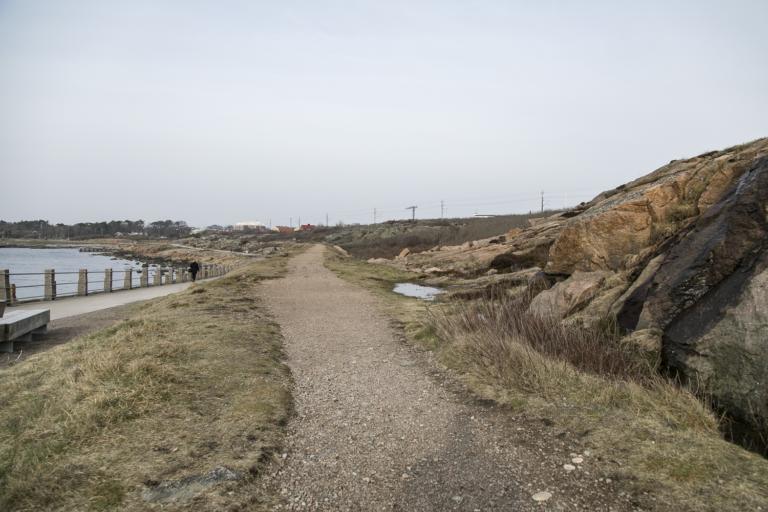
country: SE
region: Halland
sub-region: Varbergs Kommun
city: Varberg
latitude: 57.0948
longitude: 12.2413
